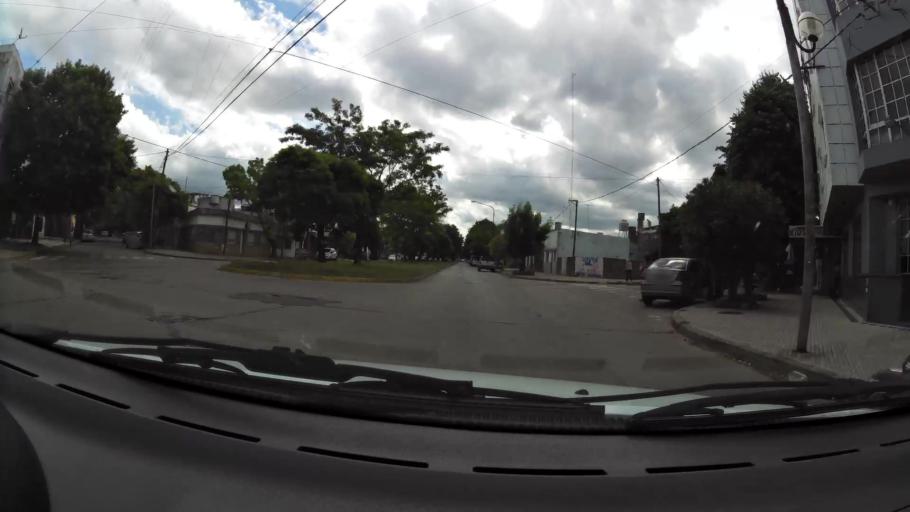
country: AR
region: Buenos Aires
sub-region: Partido de La Plata
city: La Plata
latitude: -34.9148
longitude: -57.9247
